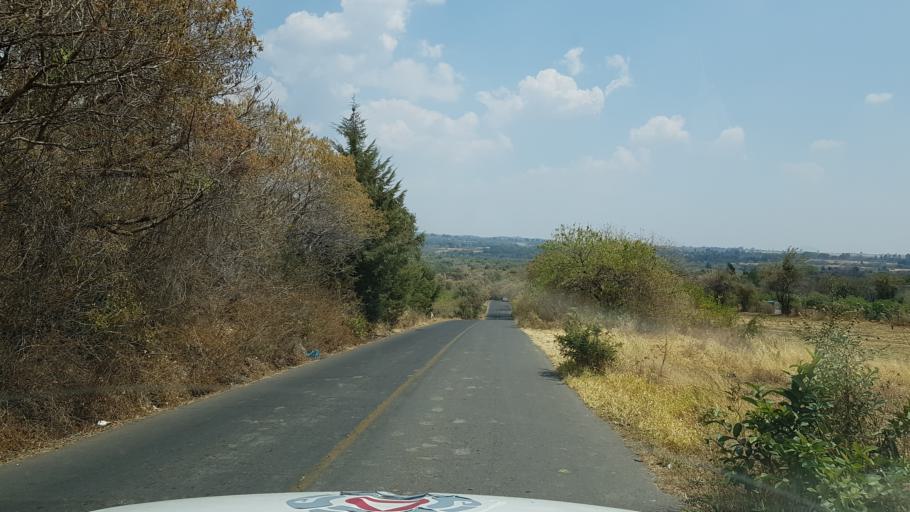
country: MX
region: Morelos
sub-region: Yecapixtla
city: Texcala
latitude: 18.8997
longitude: -98.8093
